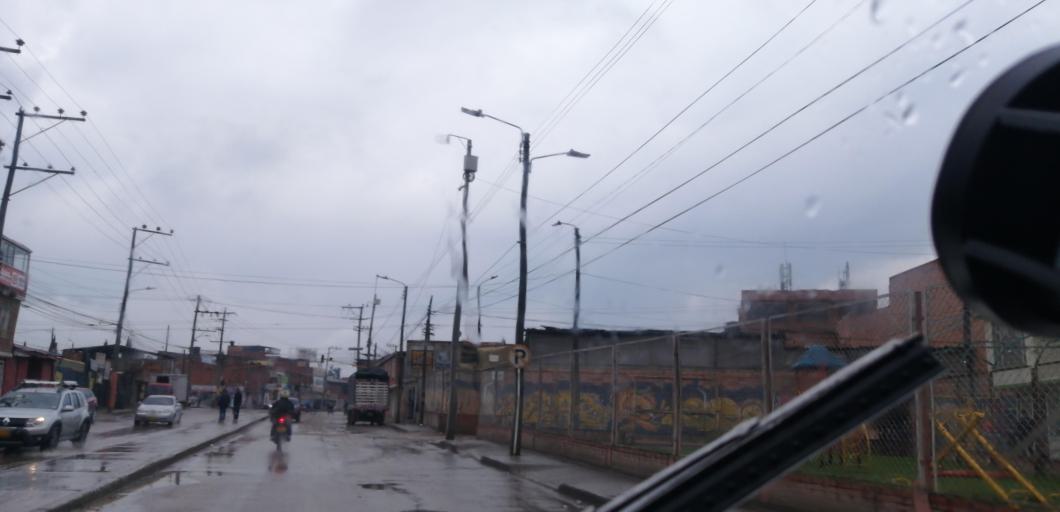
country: CO
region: Cundinamarca
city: Madrid
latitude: 4.7367
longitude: -74.2581
